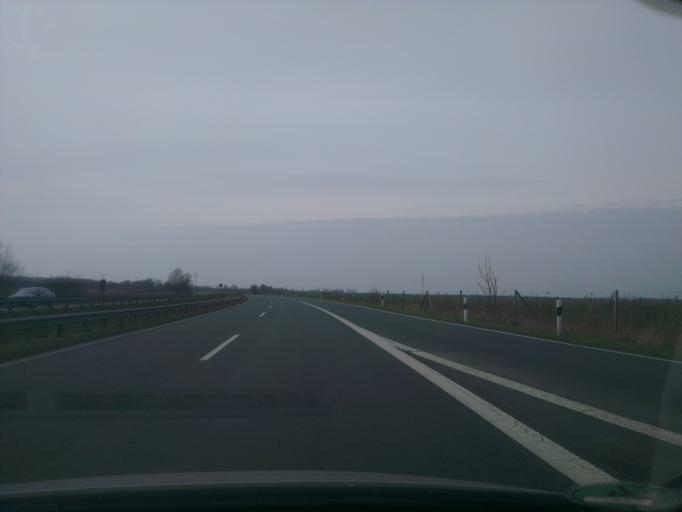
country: DE
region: Lower Saxony
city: Hinte
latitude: 53.3840
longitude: 7.1786
